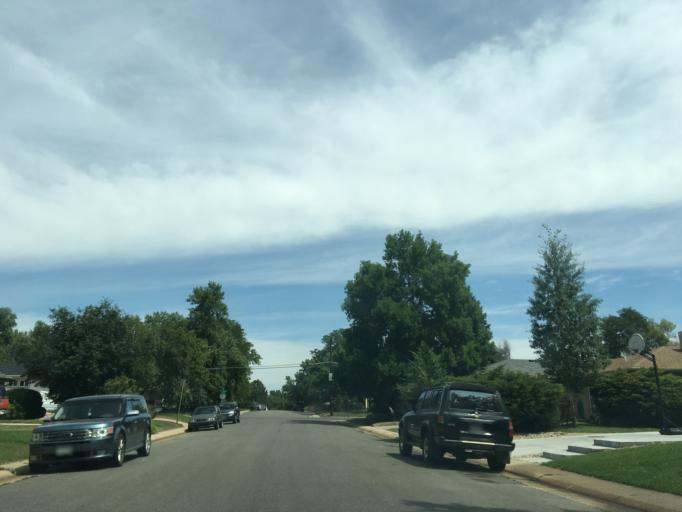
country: US
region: Colorado
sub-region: Jefferson County
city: Lakewood
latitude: 39.6923
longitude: -105.0378
